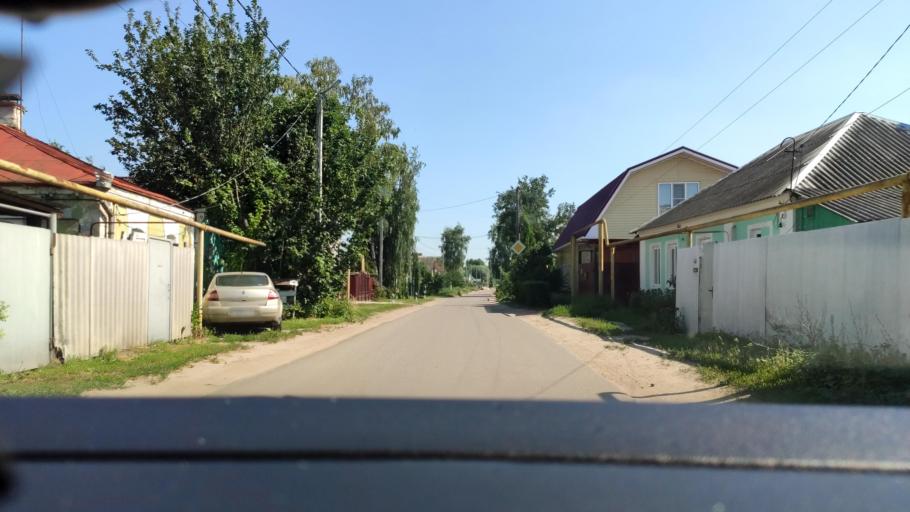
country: RU
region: Voronezj
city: Novaya Usman'
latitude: 51.6374
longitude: 39.4126
